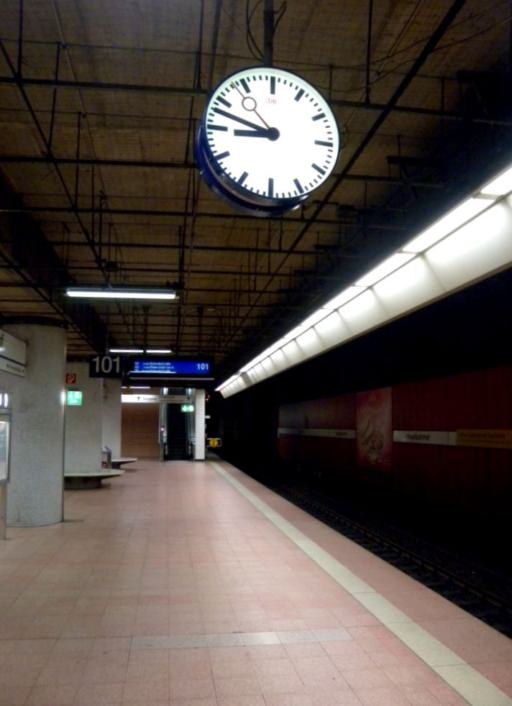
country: DE
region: Baden-Wuerttemberg
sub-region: Regierungsbezirk Stuttgart
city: Stuttgart
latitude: 48.7829
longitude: 9.1799
